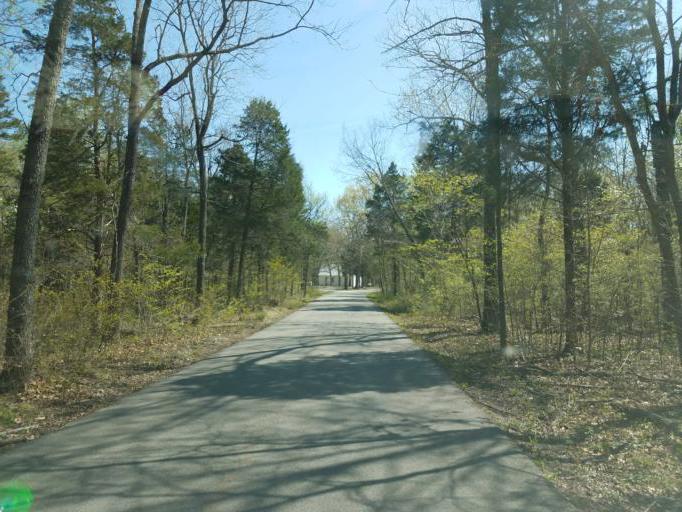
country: US
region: Kentucky
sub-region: Barren County
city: Cave City
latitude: 37.1974
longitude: -86.0757
